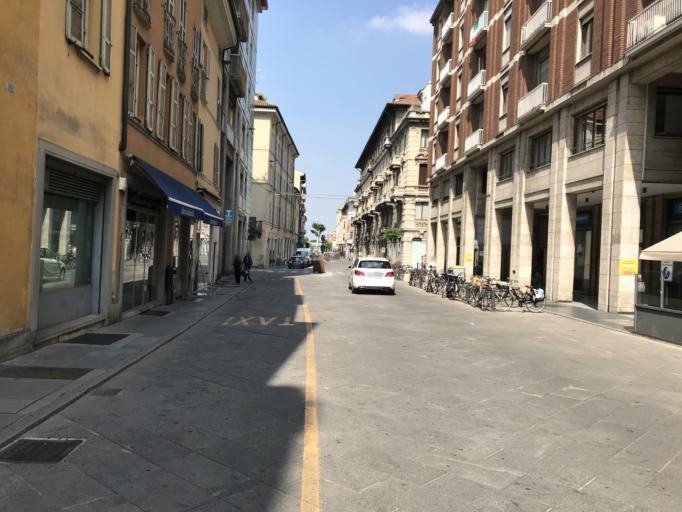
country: IT
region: Emilia-Romagna
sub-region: Provincia di Piacenza
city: Piacenza
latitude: 45.0528
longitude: 9.6938
